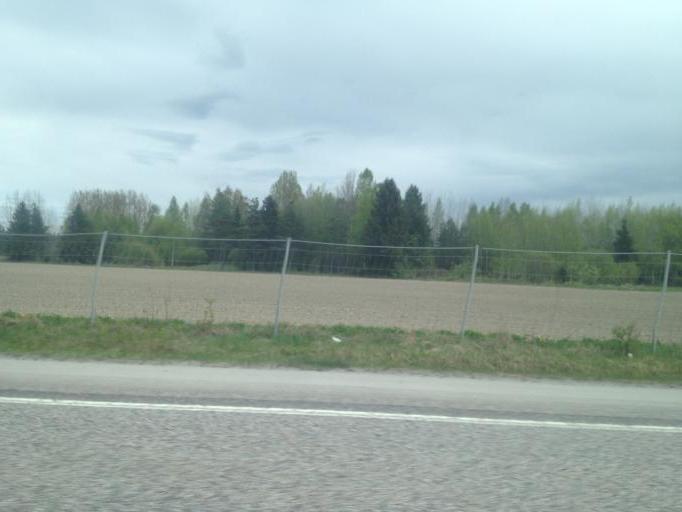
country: FI
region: Uusimaa
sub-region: Helsinki
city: Hyvinge
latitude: 60.5827
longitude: 24.8016
